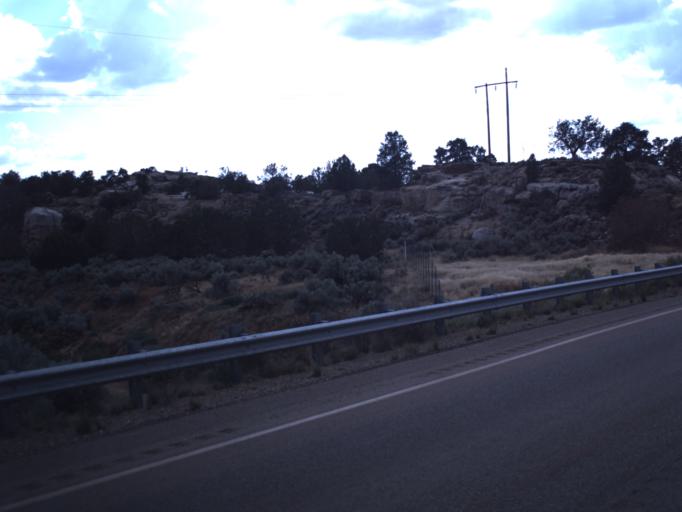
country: US
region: Utah
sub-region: Kane County
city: Kanab
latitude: 37.0404
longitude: -112.2507
